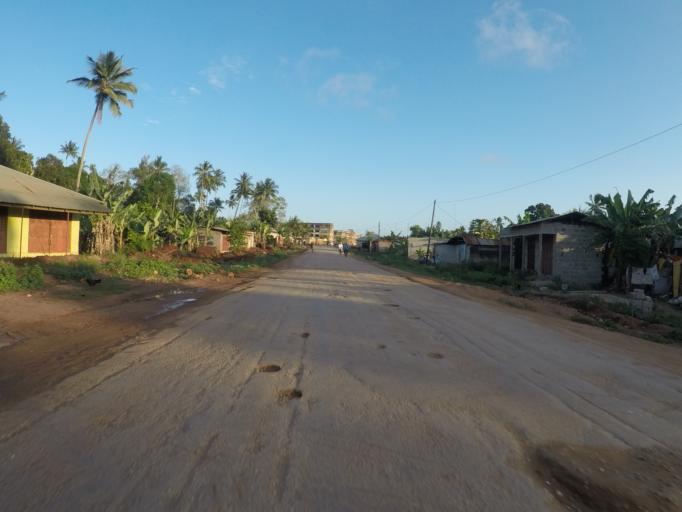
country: TZ
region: Zanzibar North
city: Gamba
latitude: -5.9065
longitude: 39.2978
